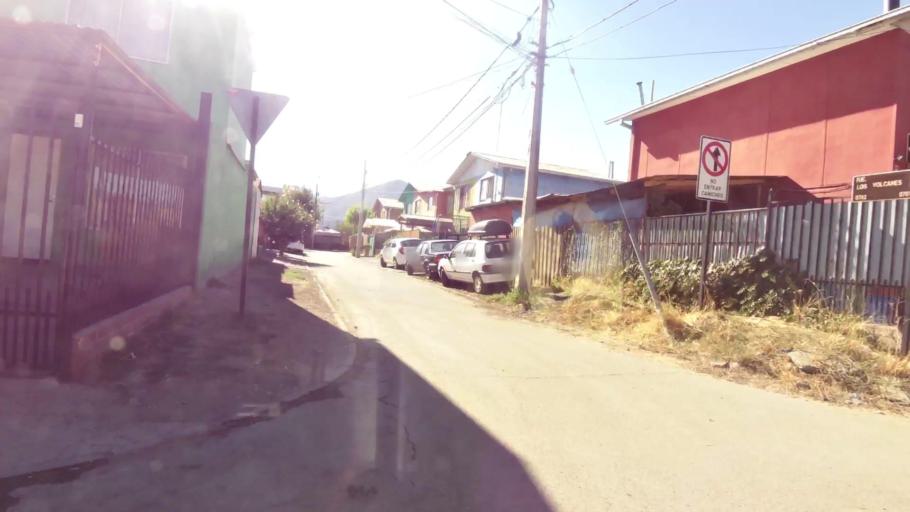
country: CL
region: O'Higgins
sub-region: Provincia de Colchagua
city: Chimbarongo
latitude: -34.5807
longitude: -71.0054
